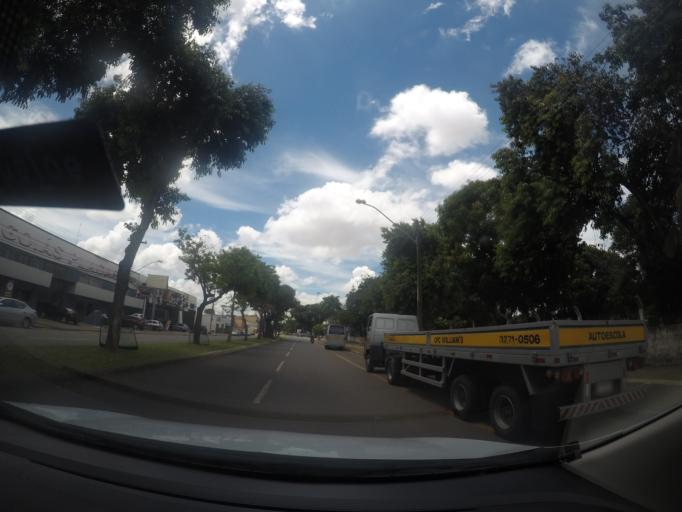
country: BR
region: Goias
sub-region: Goiania
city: Goiania
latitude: -16.6816
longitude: -49.3071
